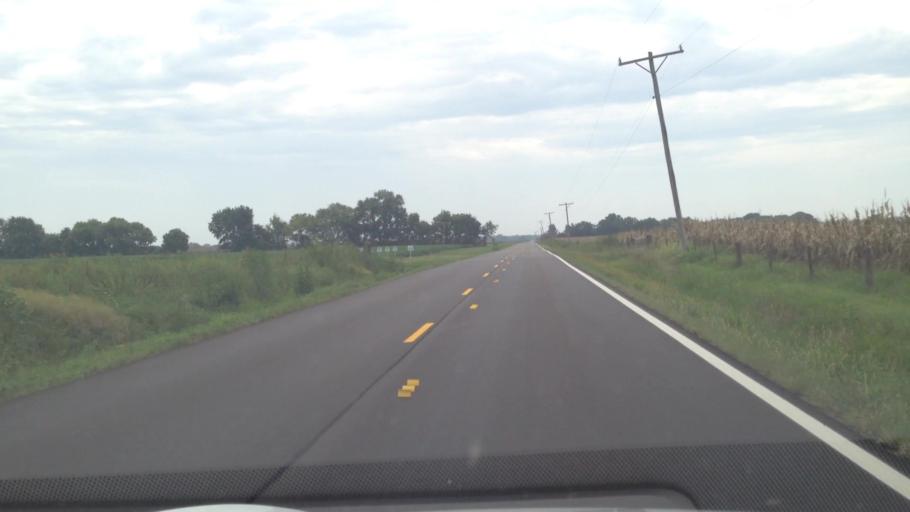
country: US
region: Kansas
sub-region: Crawford County
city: Girard
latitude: 37.6280
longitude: -94.9698
